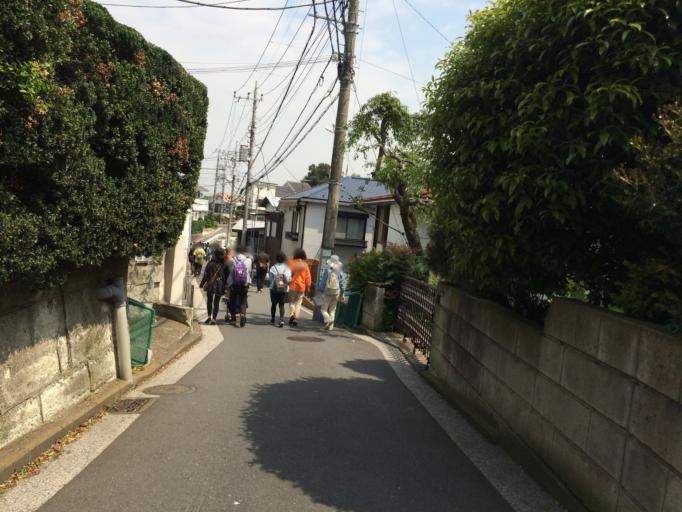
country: JP
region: Kanagawa
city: Yokohama
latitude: 35.5109
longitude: 139.6374
